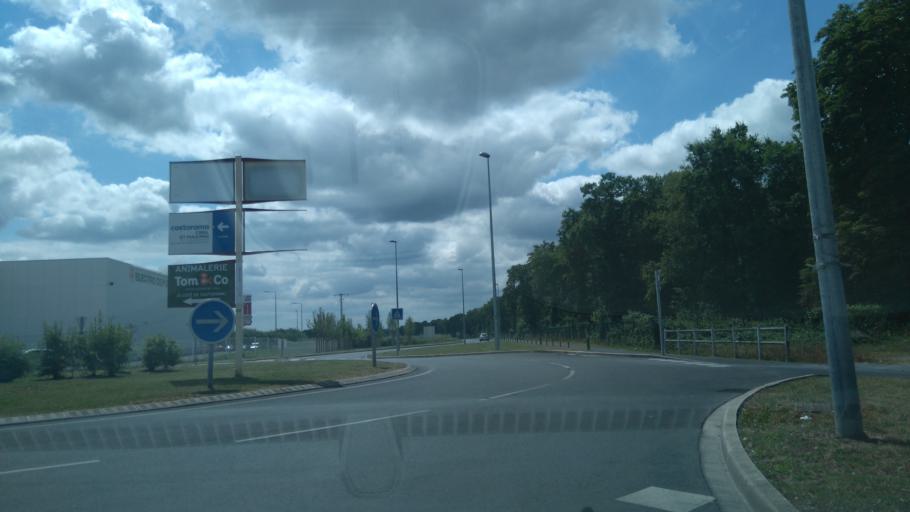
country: FR
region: Picardie
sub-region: Departement de l'Oise
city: Saint-Maximin
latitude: 49.2318
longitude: 2.4584
